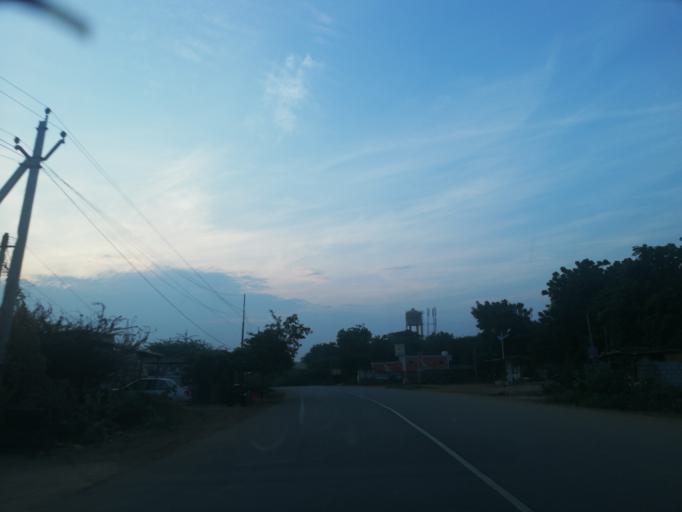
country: IN
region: Andhra Pradesh
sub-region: Guntur
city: Macherla
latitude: 16.5870
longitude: 79.3221
